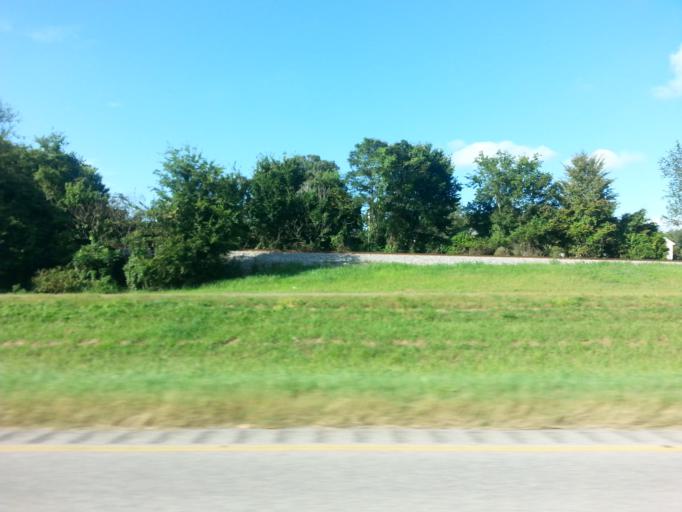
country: US
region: Alabama
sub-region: Colbert County
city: Tuscumbia
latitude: 34.7106
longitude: -87.7714
